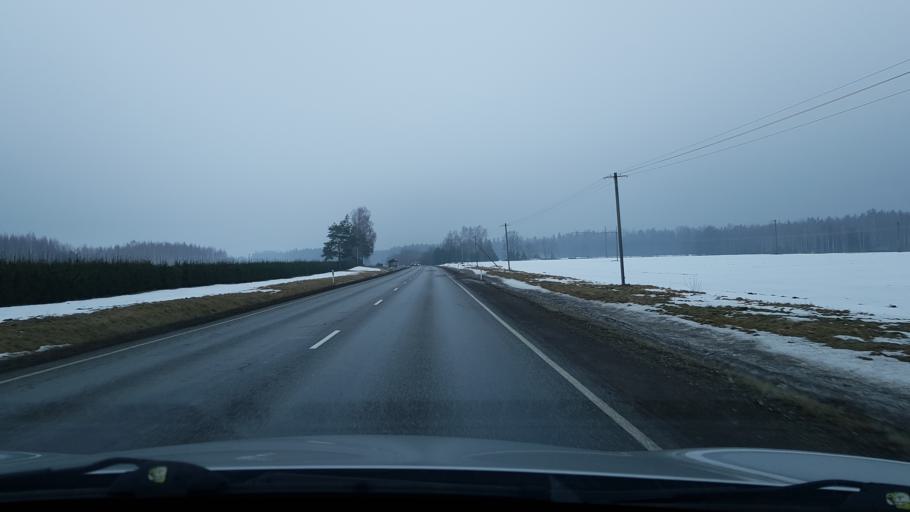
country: EE
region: Valgamaa
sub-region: Valga linn
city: Valga
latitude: 57.9016
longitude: 26.1712
